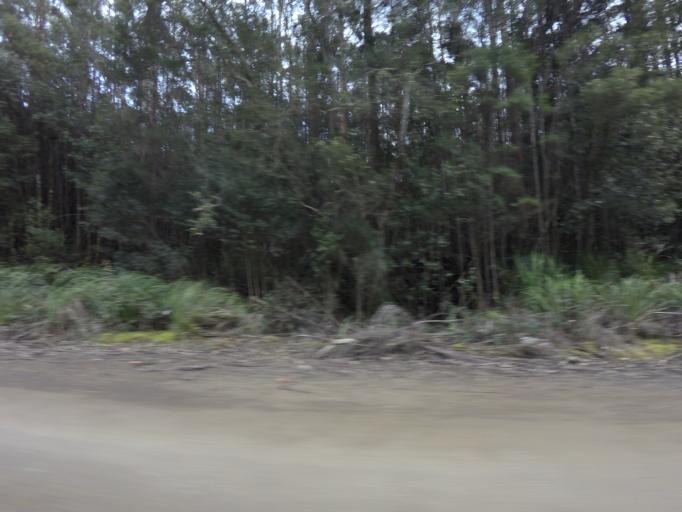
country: AU
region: Tasmania
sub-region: Huon Valley
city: Geeveston
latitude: -43.5214
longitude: 146.8821
